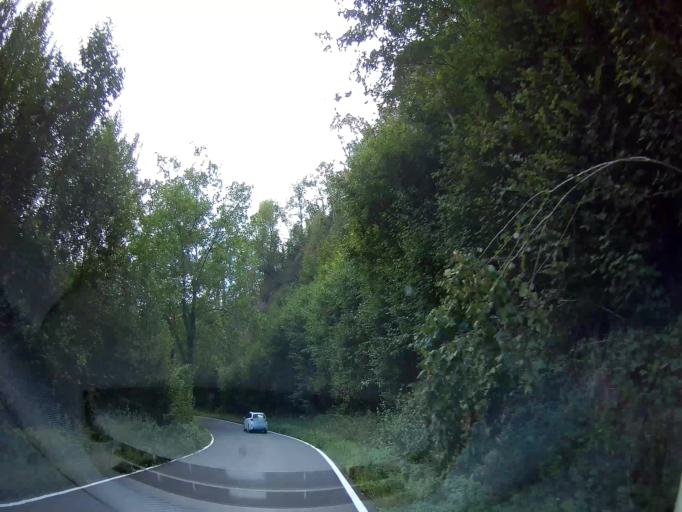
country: BE
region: Wallonia
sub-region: Province de Namur
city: Onhaye
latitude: 50.2973
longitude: 4.8142
